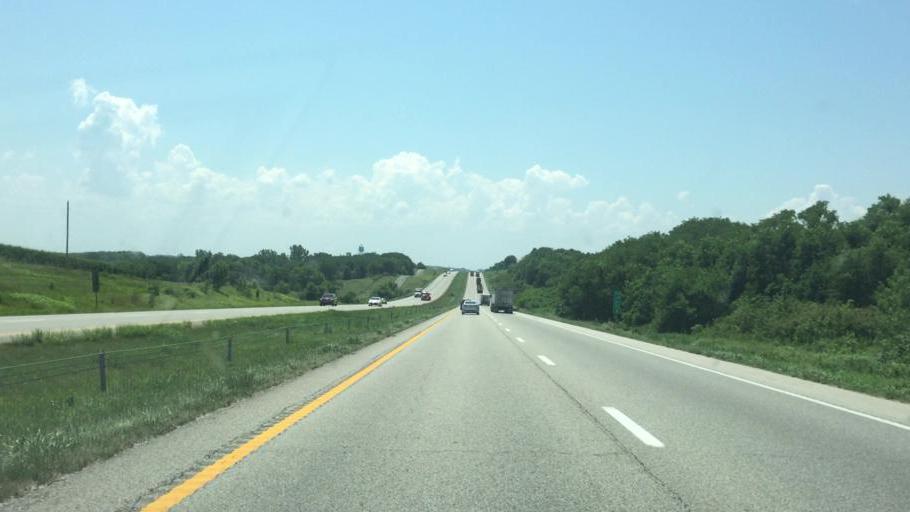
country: US
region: Missouri
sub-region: Platte County
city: Platte City
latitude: 39.5437
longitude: -94.7878
